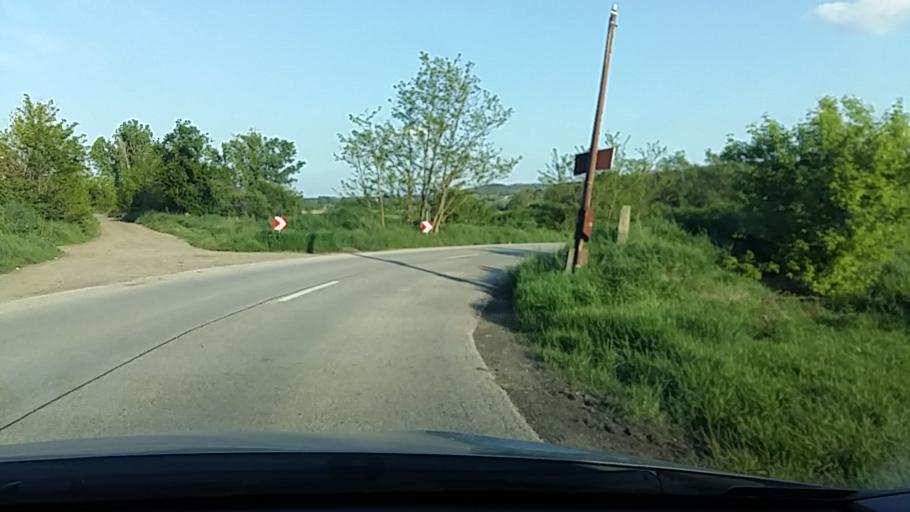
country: HU
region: Pest
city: Szod
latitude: 47.7592
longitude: 19.1885
